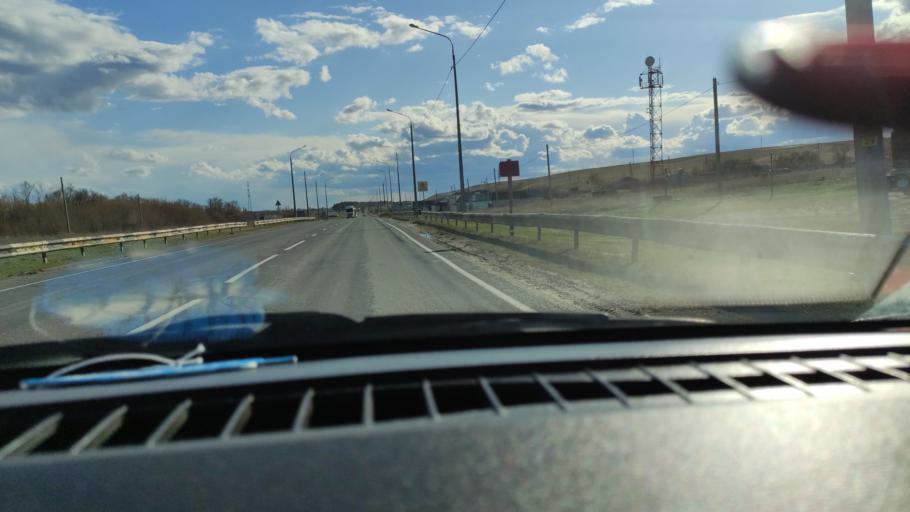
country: RU
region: Saratov
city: Sinodskoye
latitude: 52.0834
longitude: 46.7987
